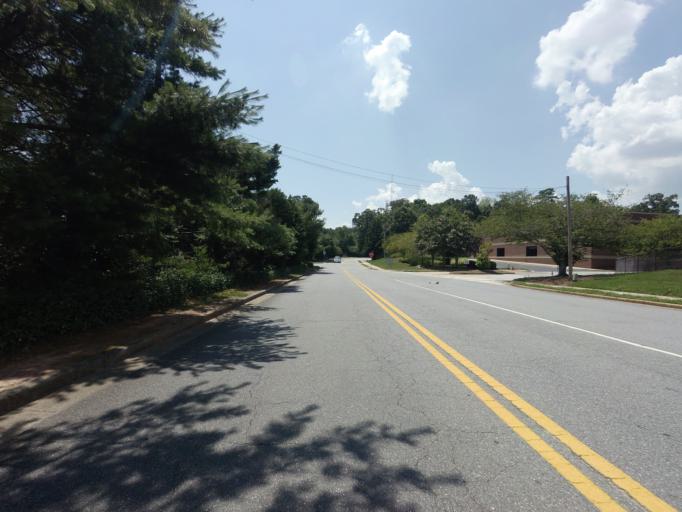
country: US
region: Georgia
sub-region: Fulton County
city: Johns Creek
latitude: 34.0408
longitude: -84.2227
